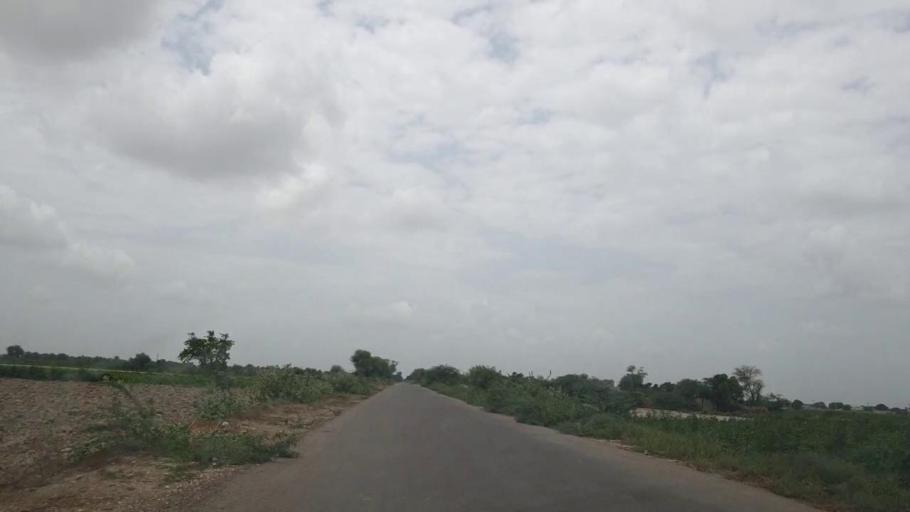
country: PK
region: Sindh
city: Naukot
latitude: 24.9003
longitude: 69.2599
